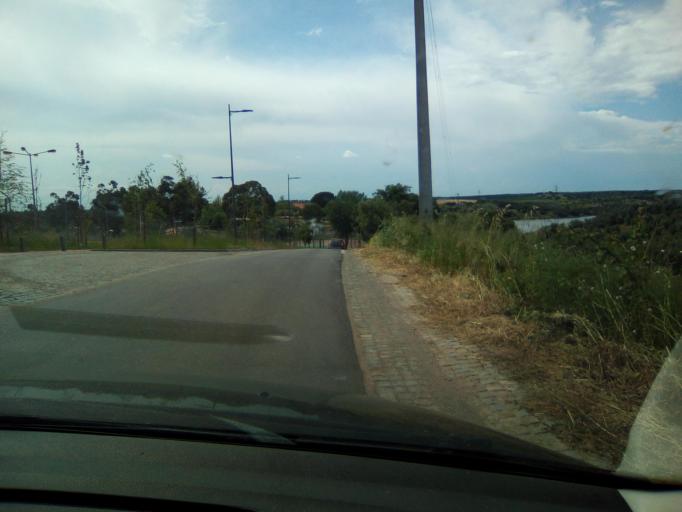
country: PT
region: Portalegre
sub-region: Avis
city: Avis
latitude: 39.0552
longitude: -7.9078
